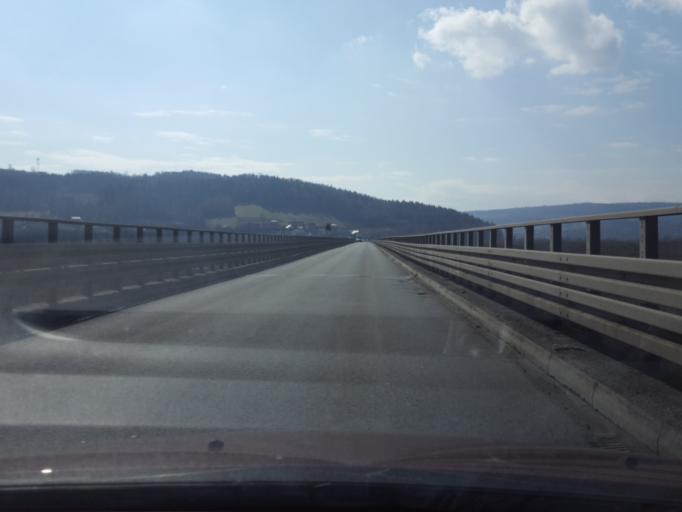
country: PL
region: Lesser Poland Voivodeship
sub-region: Powiat nowosadecki
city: Chelmiec
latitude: 49.6908
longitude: 20.6544
